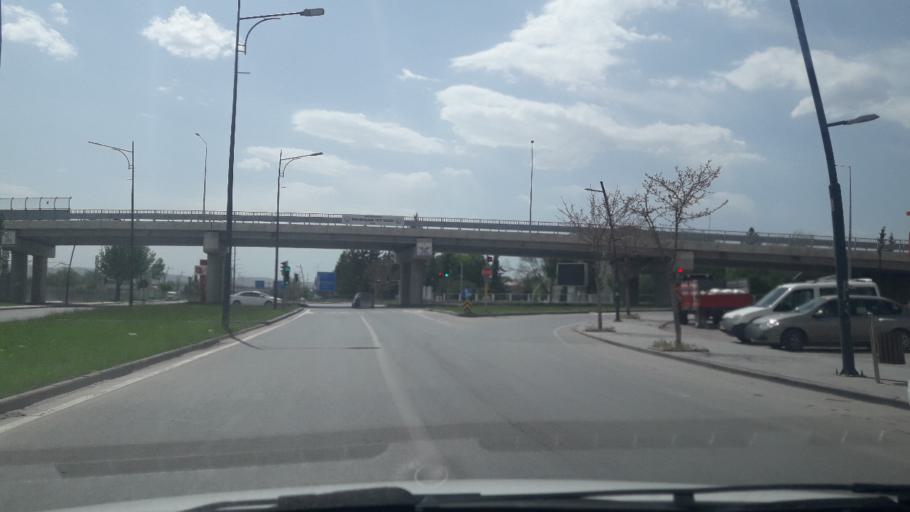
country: TR
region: Sivas
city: Sivas
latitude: 39.7260
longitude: 36.9697
